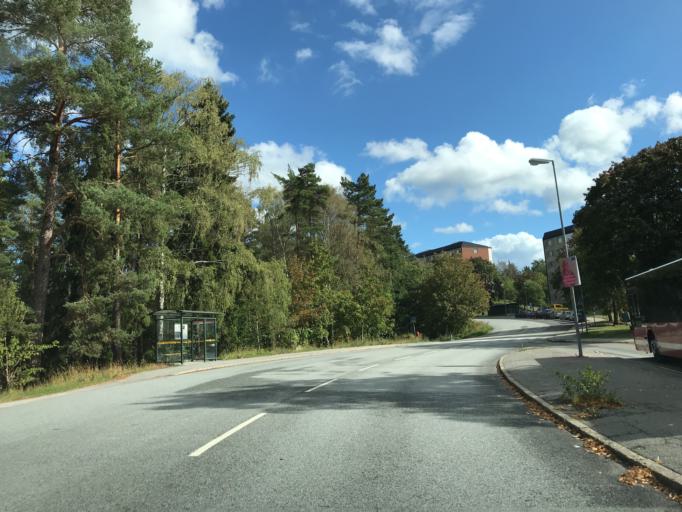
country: SE
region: Stockholm
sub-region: Sollentuna Kommun
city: Sollentuna
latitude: 59.4487
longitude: 17.9697
